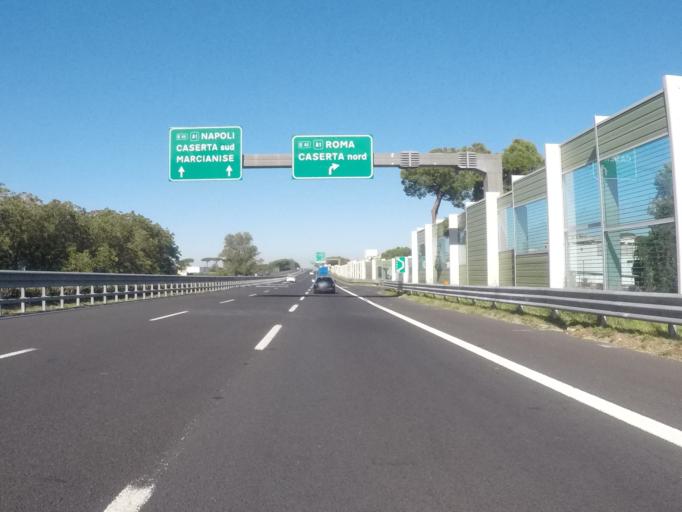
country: IT
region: Campania
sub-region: Provincia di Caserta
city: San Marco Evangelista
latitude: 41.0344
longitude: 14.3325
